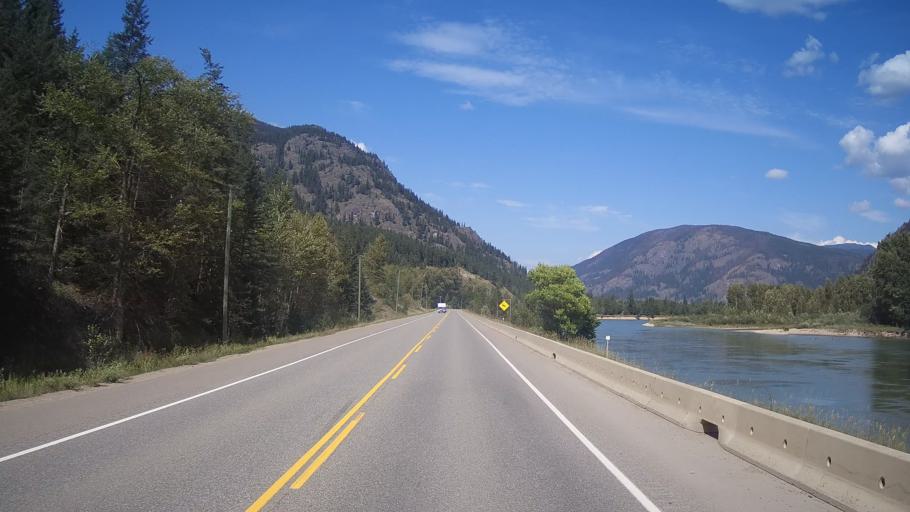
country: CA
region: British Columbia
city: Kamloops
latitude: 51.4337
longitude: -120.1940
